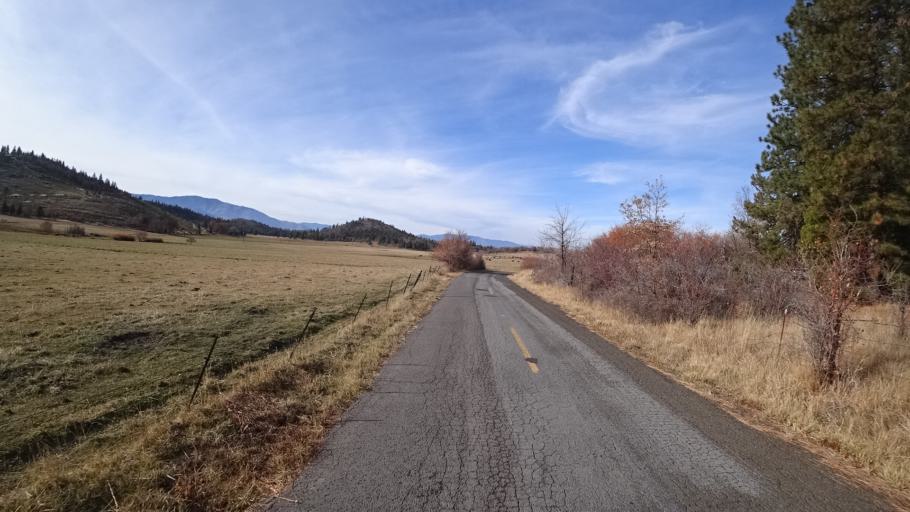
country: US
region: California
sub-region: Siskiyou County
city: Weed
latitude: 41.4495
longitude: -122.3805
